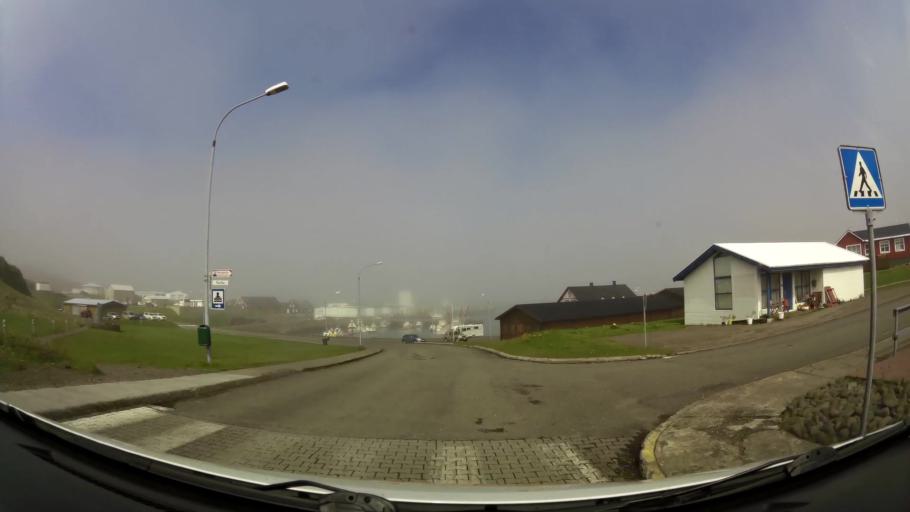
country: IS
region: East
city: Reydarfjoerdur
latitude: 64.6555
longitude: -14.2810
